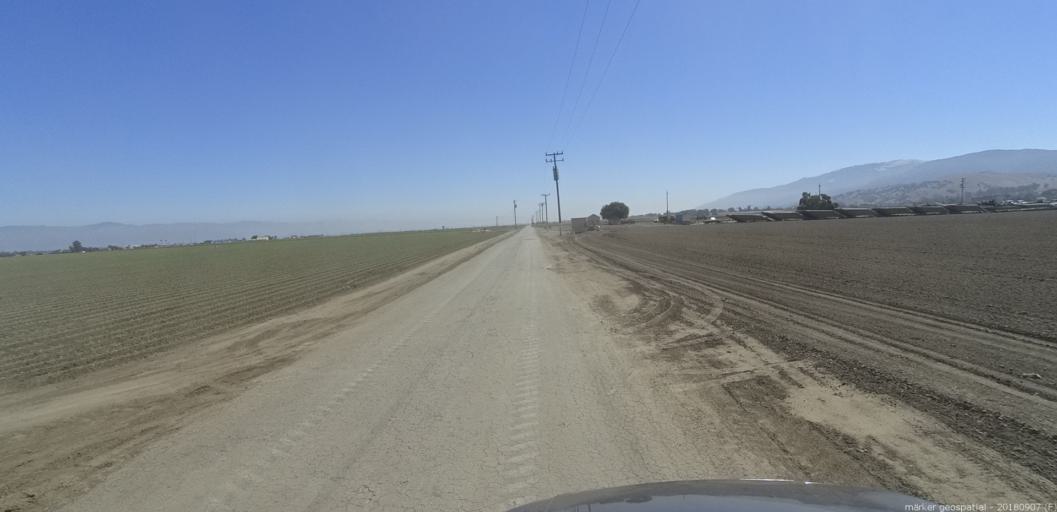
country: US
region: California
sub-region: Monterey County
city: Salinas
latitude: 36.6428
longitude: -121.6815
